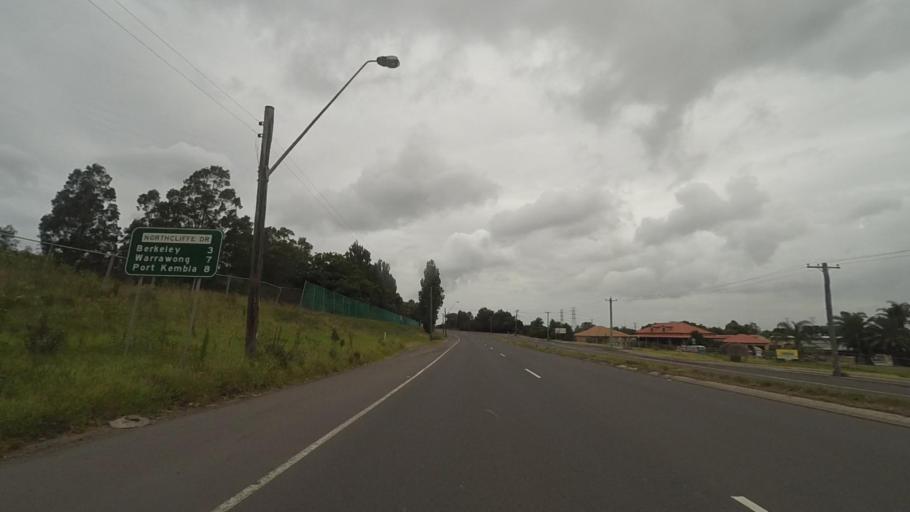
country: AU
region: New South Wales
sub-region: Wollongong
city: Berkeley
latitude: -34.4701
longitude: 150.8276
